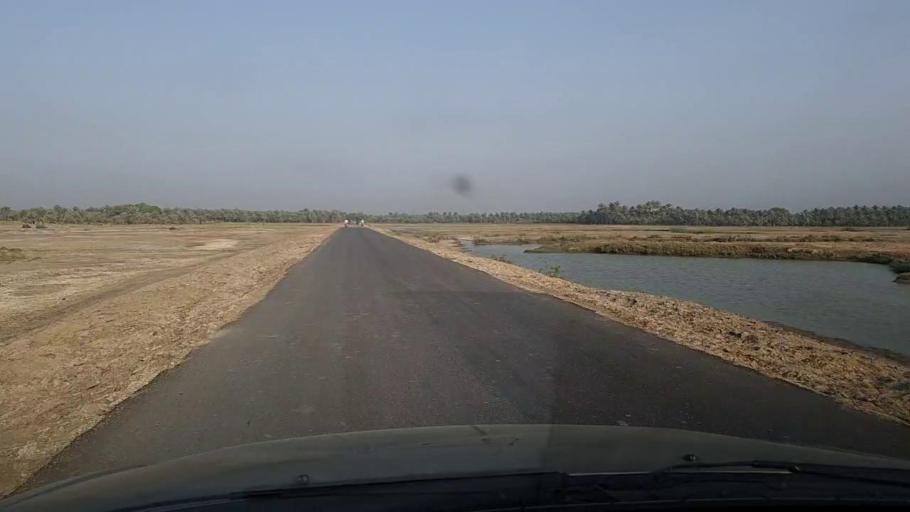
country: PK
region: Sindh
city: Pir jo Goth
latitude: 27.5595
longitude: 68.6672
